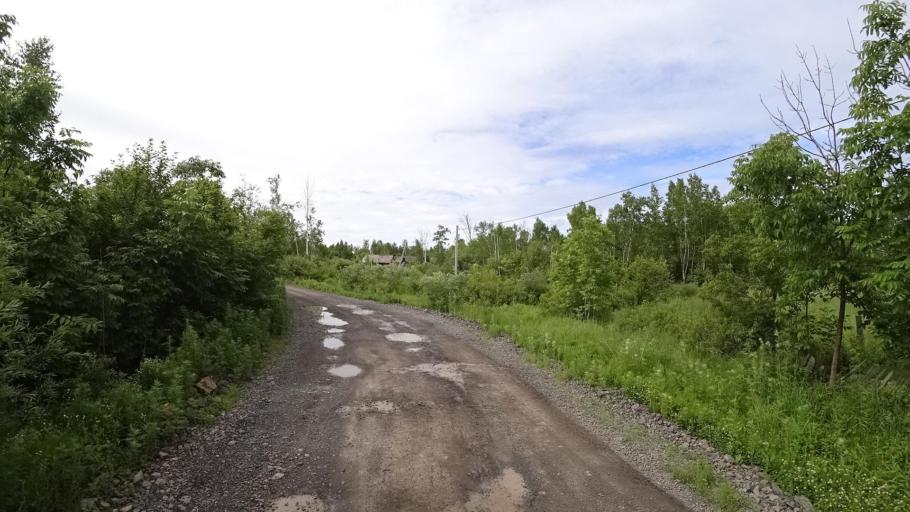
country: RU
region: Khabarovsk Krai
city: Amursk
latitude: 49.8988
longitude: 136.1491
